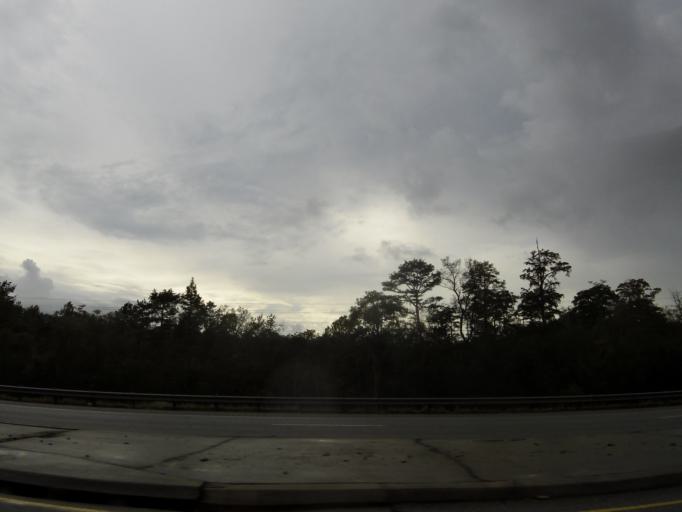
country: US
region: Georgia
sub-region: Wayne County
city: Jesup
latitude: 31.5683
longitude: -81.8404
